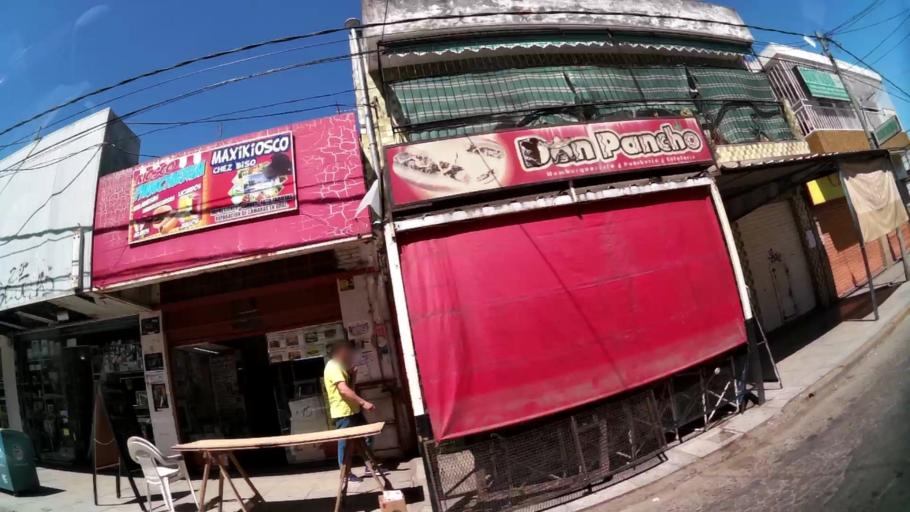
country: AR
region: Buenos Aires
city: Hurlingham
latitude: -34.5034
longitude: -58.6672
